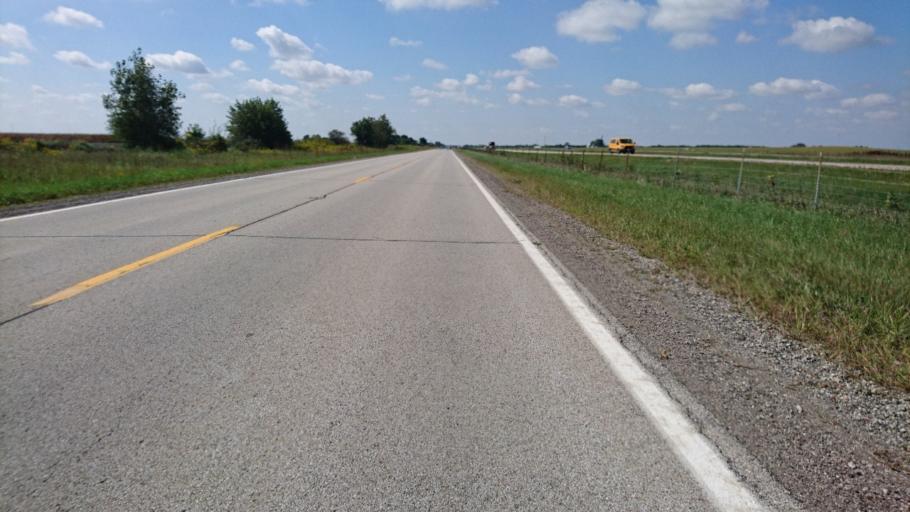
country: US
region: Illinois
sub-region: McLean County
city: Lexington
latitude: 40.6166
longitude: -88.8218
